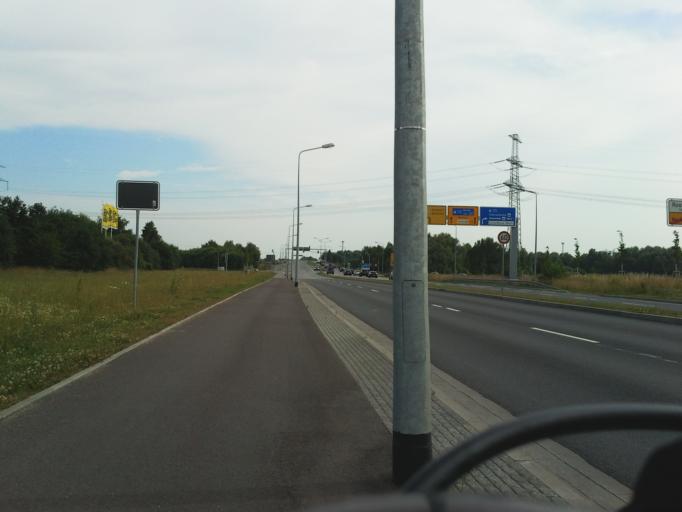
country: DE
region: Mecklenburg-Vorpommern
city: Dierkow-Neu
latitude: 54.1233
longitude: 12.1663
